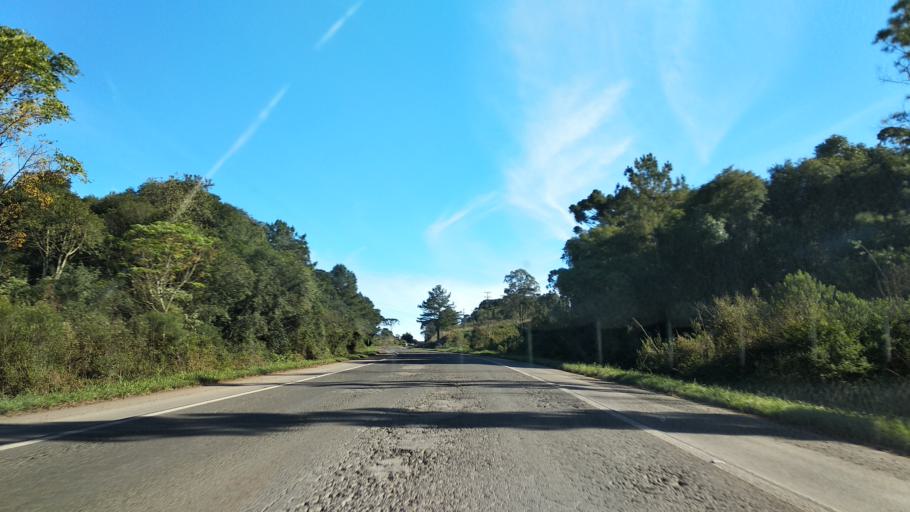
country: BR
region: Santa Catarina
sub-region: Campos Novos
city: Campos Novos
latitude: -27.4016
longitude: -51.2027
